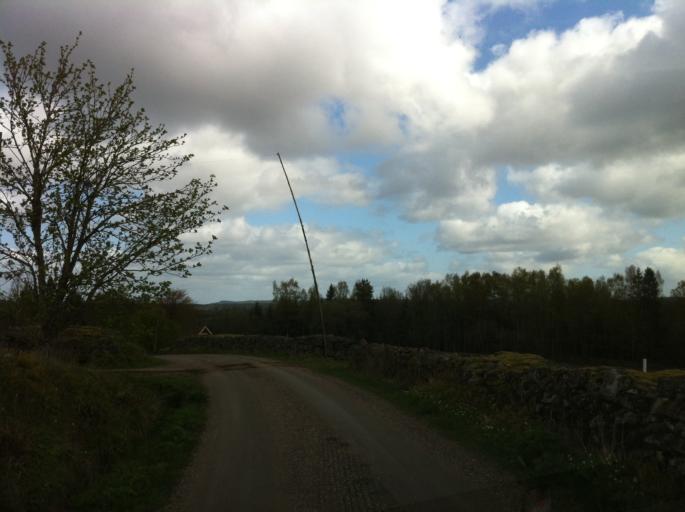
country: SE
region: Vaestra Goetaland
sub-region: Alingsas Kommun
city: Ingared
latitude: 57.8201
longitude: 12.5676
